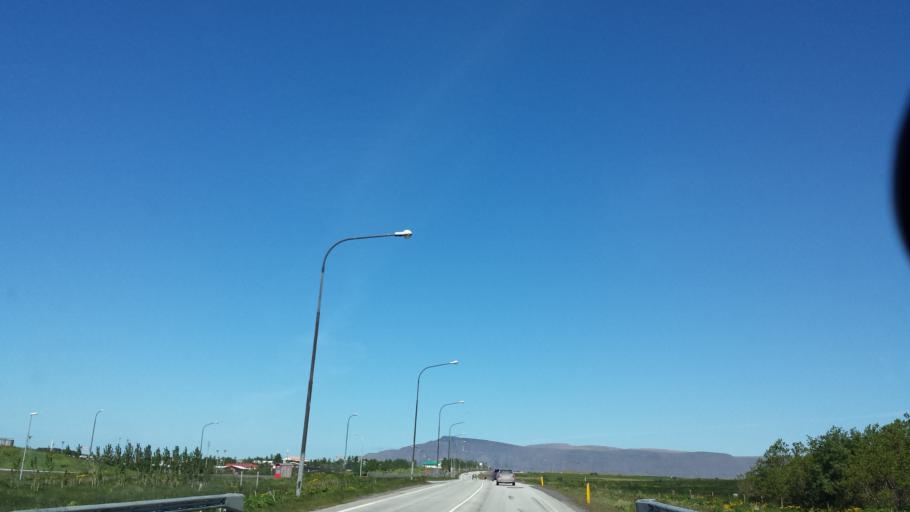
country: IS
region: Capital Region
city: Reykjavik
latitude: 64.2370
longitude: -21.8219
